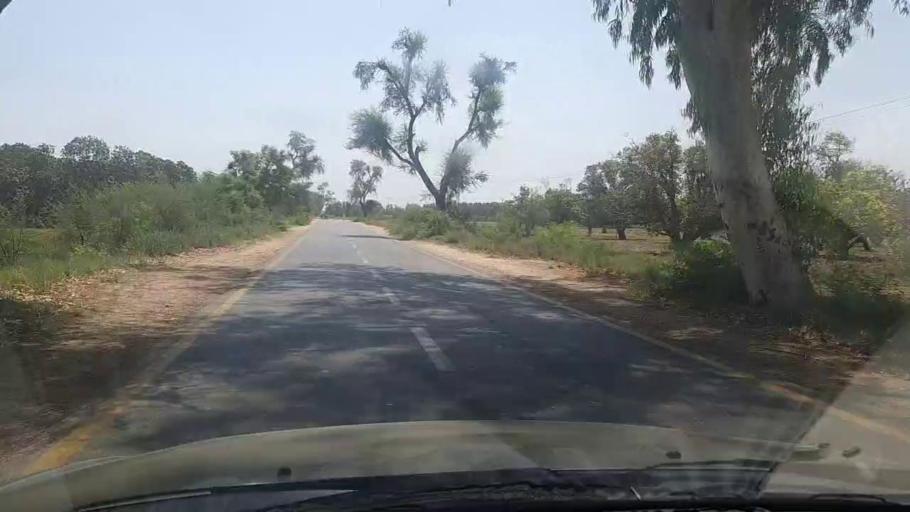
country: PK
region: Sindh
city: Tando Jam
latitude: 25.3261
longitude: 68.5474
